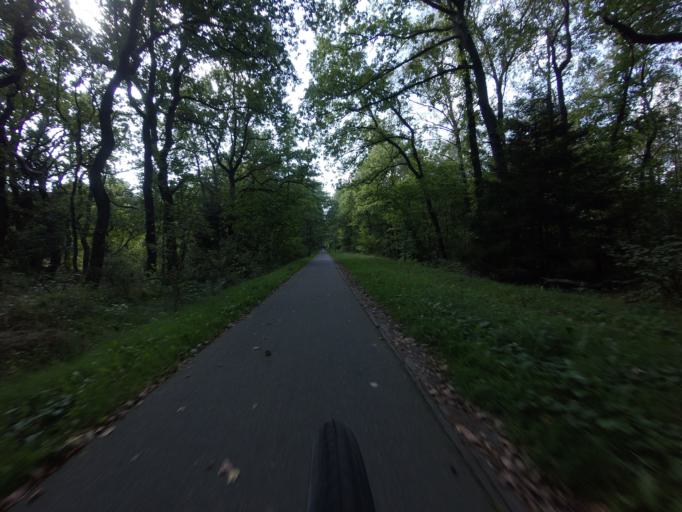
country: DK
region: Central Jutland
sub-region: Viborg Kommune
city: Viborg
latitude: 56.4064
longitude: 9.3584
